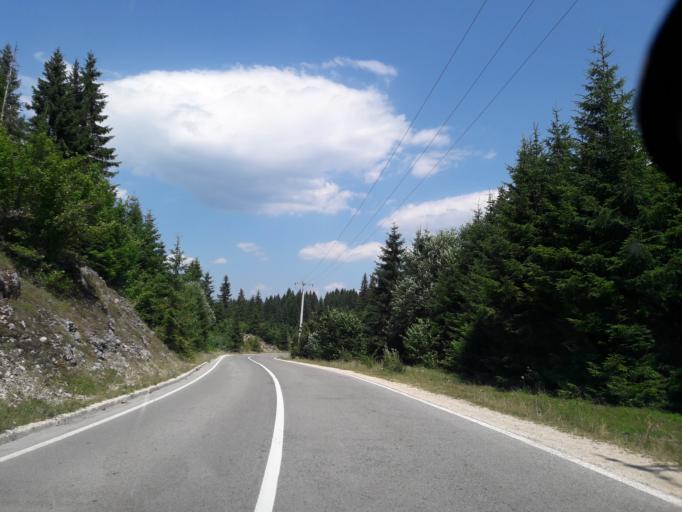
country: BA
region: Republika Srpska
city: Sipovo
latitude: 44.1233
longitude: 17.1810
